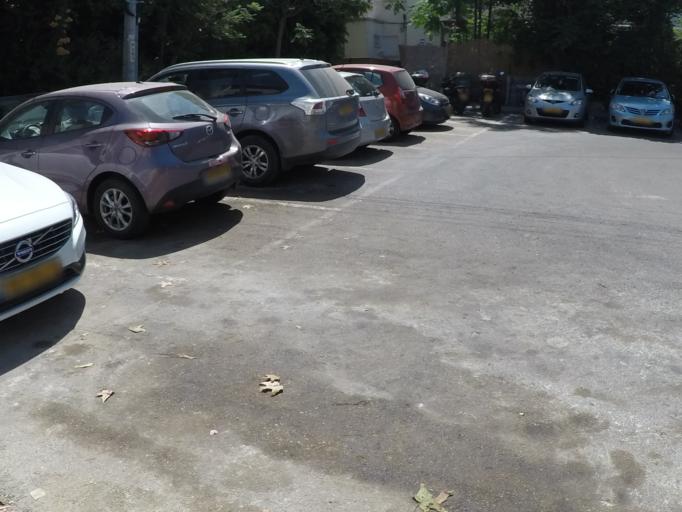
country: IL
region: Tel Aviv
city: Ramat Gan
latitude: 32.1066
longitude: 34.7995
